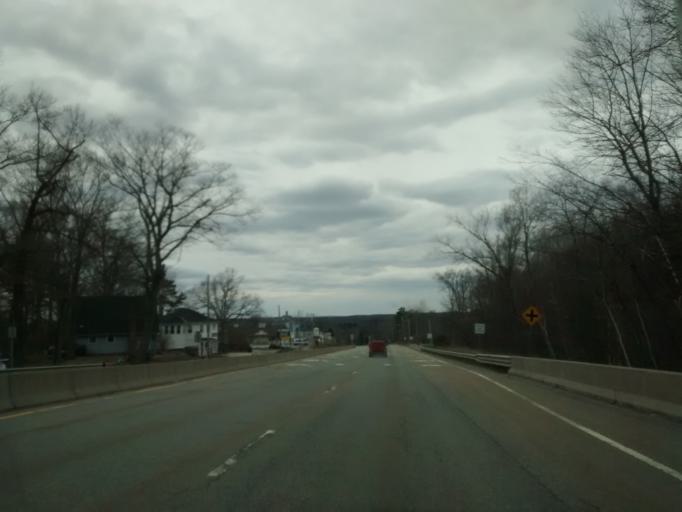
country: US
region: Massachusetts
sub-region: Worcester County
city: Charlton
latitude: 42.1467
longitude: -71.9748
